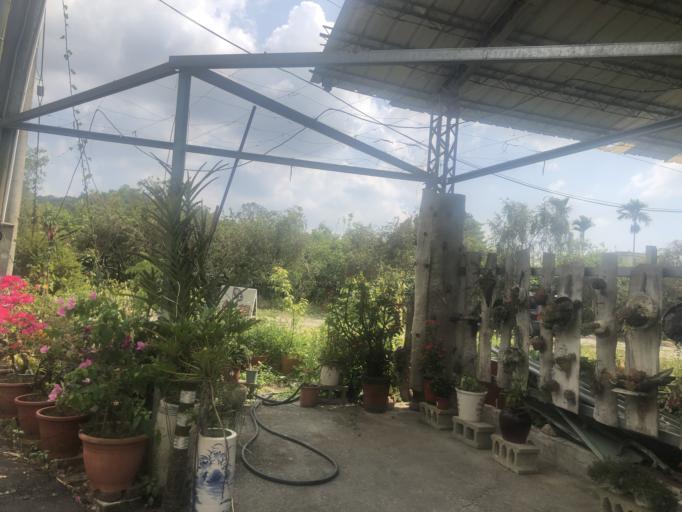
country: TW
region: Taiwan
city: Fengyuan
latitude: 24.2002
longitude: 120.8412
